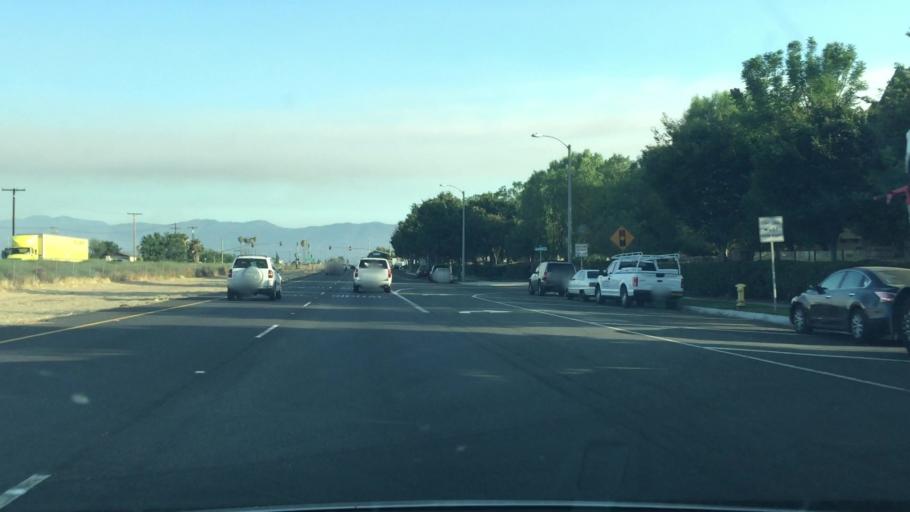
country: US
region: California
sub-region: San Bernardino County
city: Chino
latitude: 34.0146
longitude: -117.6509
